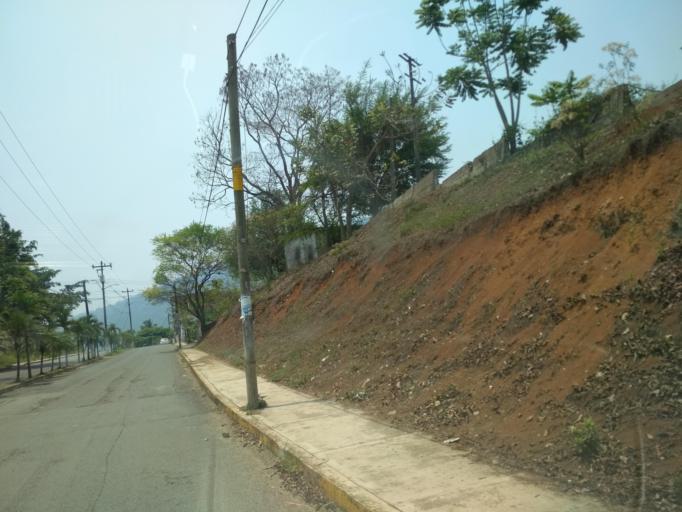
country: MX
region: Veracruz
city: Tezonapa
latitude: 18.6077
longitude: -96.6893
